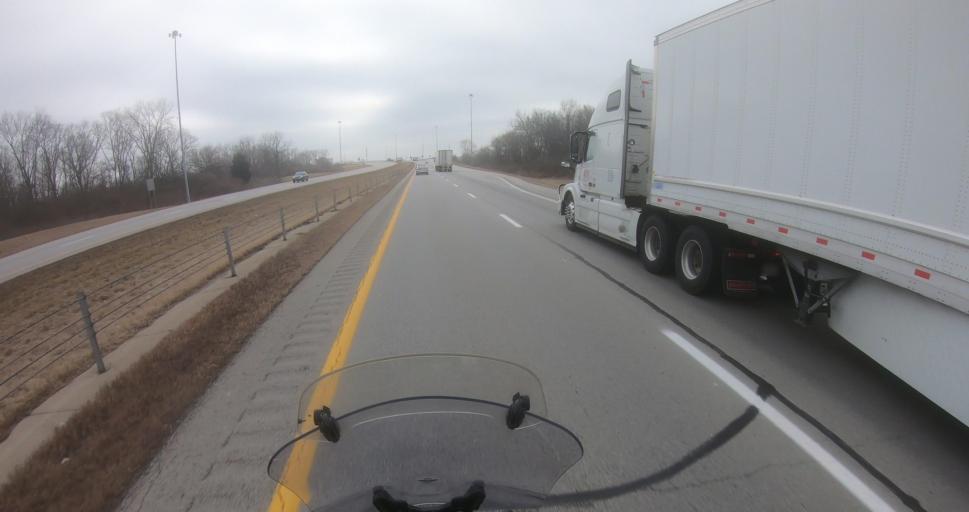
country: US
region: Ohio
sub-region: Miami County
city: Piqua
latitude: 40.1719
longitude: -84.2206
